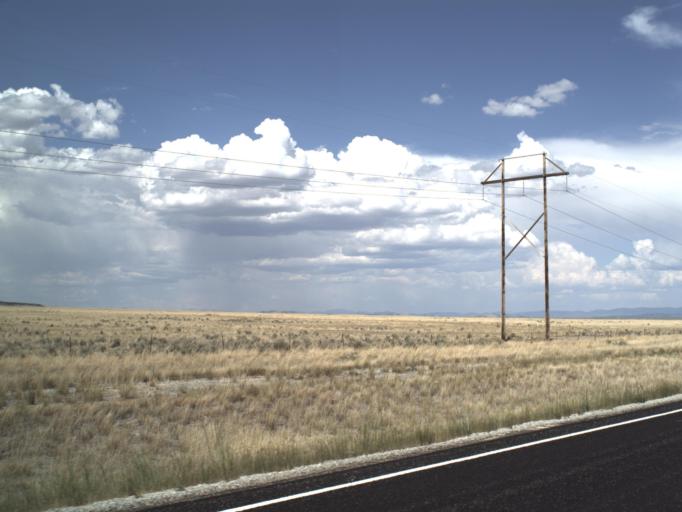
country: US
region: Idaho
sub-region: Power County
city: American Falls
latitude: 41.9689
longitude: -113.1054
